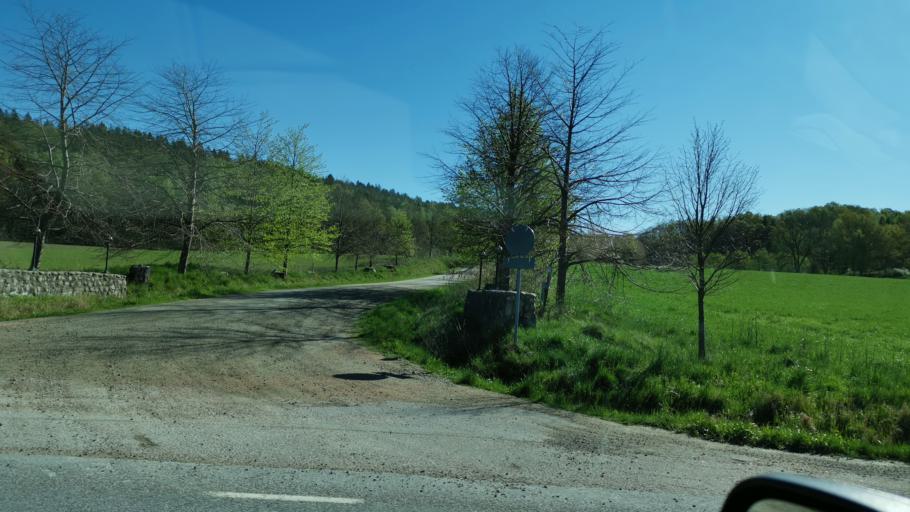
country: SE
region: Vaestra Goetaland
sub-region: Uddevalla Kommun
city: Ljungskile
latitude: 58.2508
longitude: 11.9055
